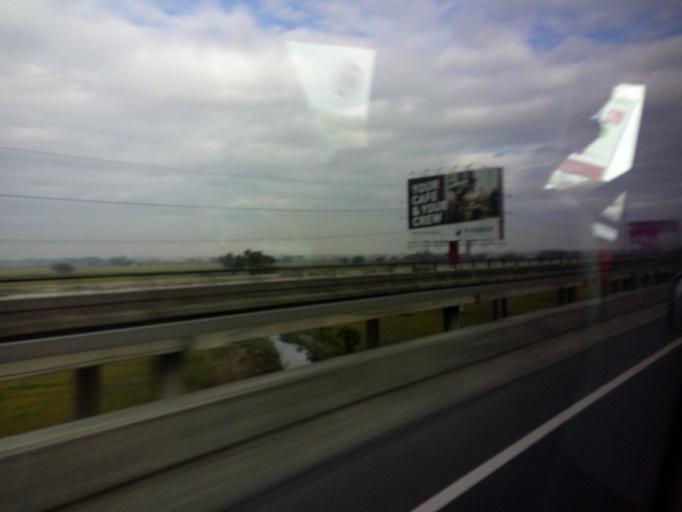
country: PH
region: Central Luzon
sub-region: Province of Pampanga
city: Balucuc
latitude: 14.9296
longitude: 120.7984
